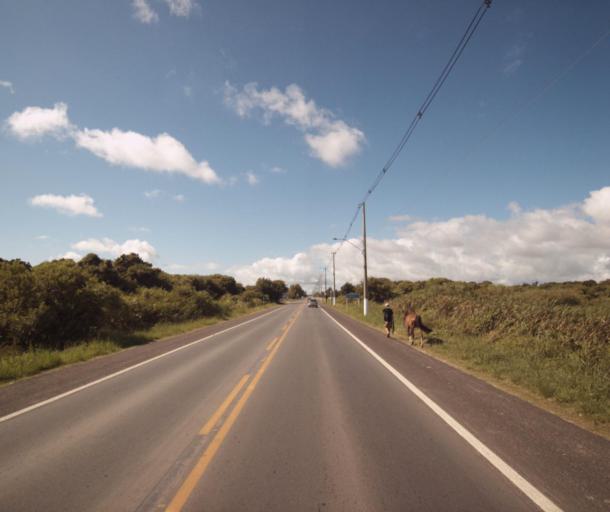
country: BR
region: Rio Grande do Sul
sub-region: Pelotas
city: Pelotas
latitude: -31.7517
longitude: -52.3594
